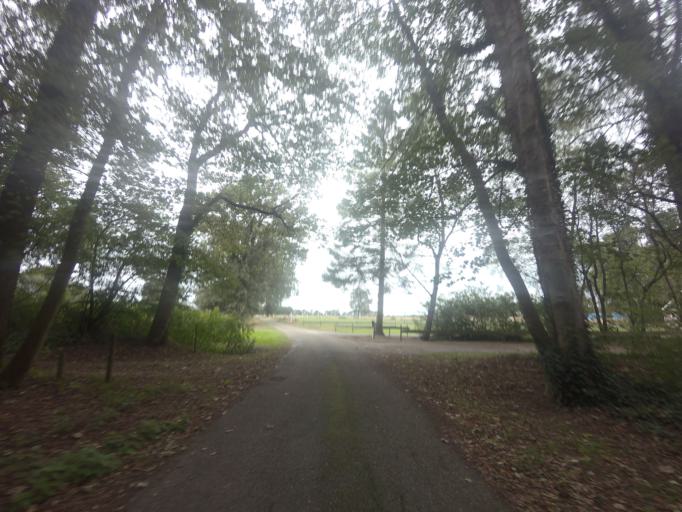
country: NL
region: Drenthe
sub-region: Gemeente Westerveld
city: Dwingeloo
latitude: 52.9526
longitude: 6.3123
